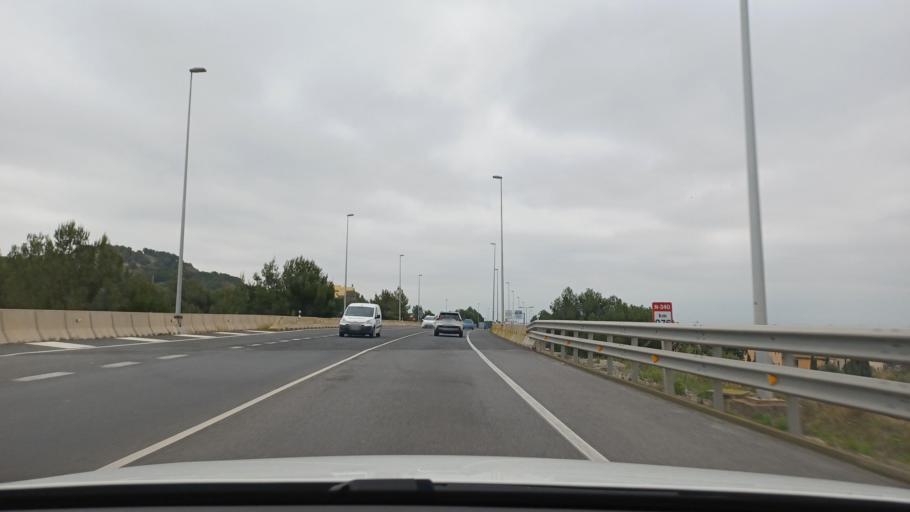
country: ES
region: Valencia
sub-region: Provincia de Castello
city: Borriol
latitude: 40.0030
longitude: -0.0805
